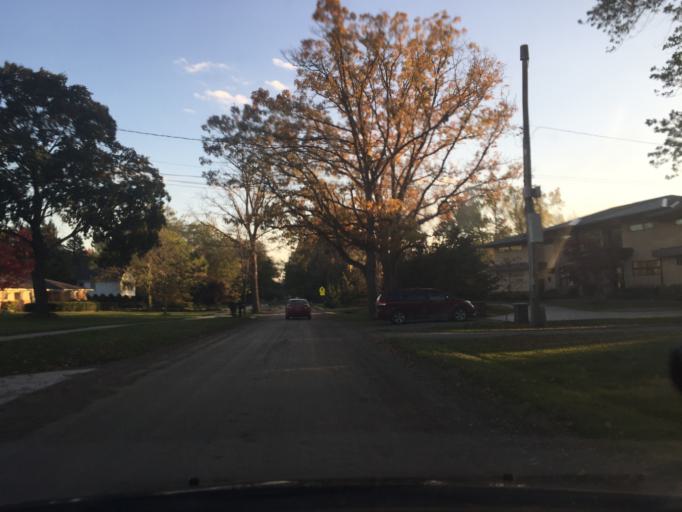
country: US
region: Michigan
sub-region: Oakland County
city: Franklin
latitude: 42.5643
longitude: -83.2948
